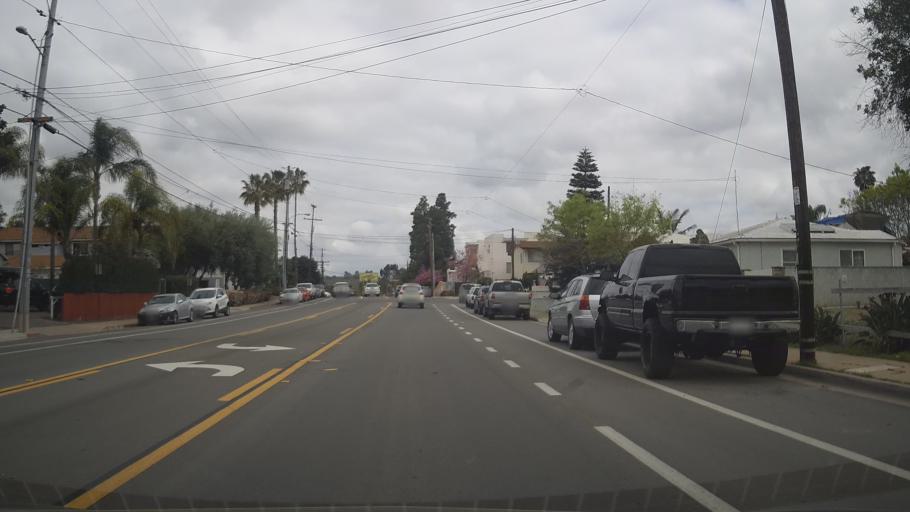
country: US
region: California
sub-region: San Diego County
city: La Mesa
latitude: 32.7653
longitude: -117.0469
